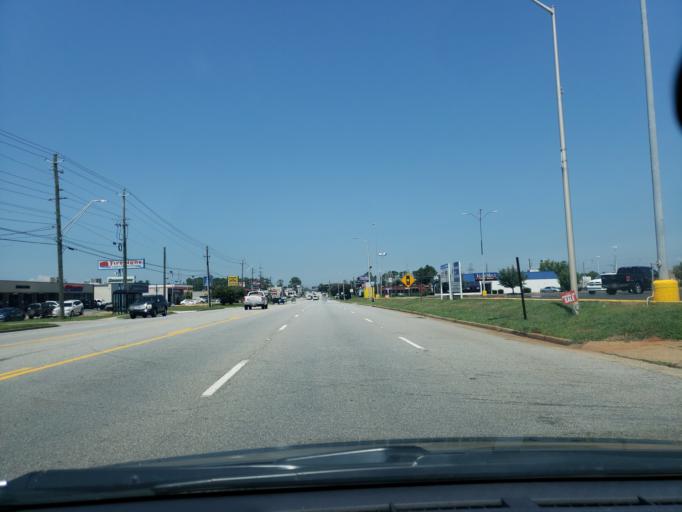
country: US
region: Georgia
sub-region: Dougherty County
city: Albany
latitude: 31.6116
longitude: -84.2131
